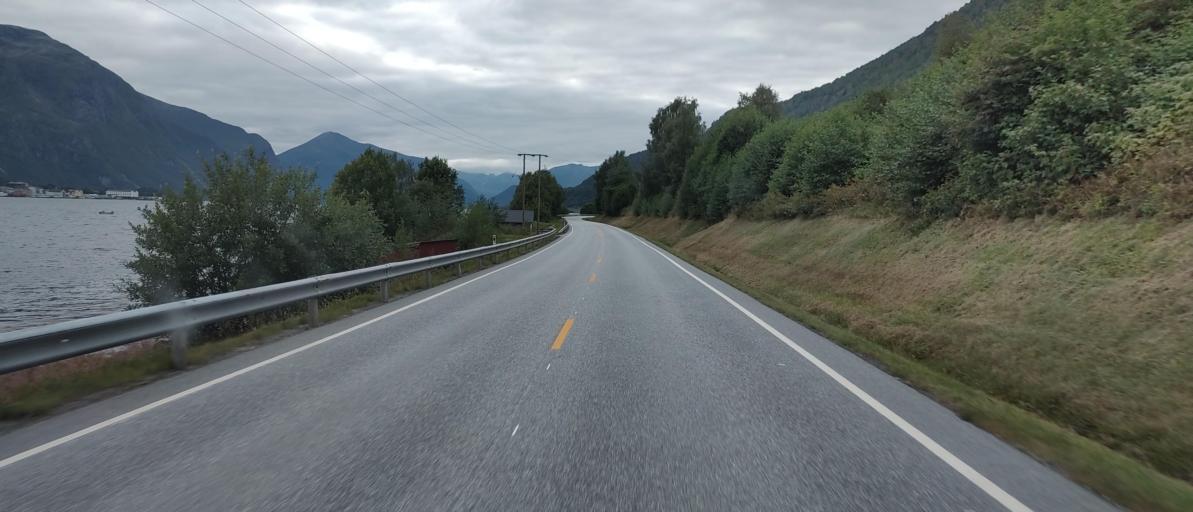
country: NO
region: More og Romsdal
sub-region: Rauma
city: Andalsnes
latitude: 62.5831
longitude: 7.7135
